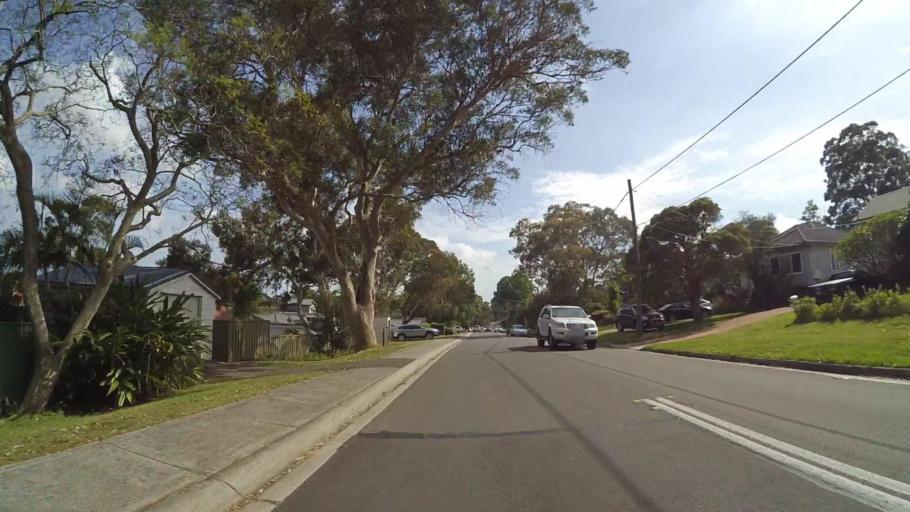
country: AU
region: New South Wales
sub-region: Sutherland Shire
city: Caringbah
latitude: -34.0436
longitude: 151.1154
